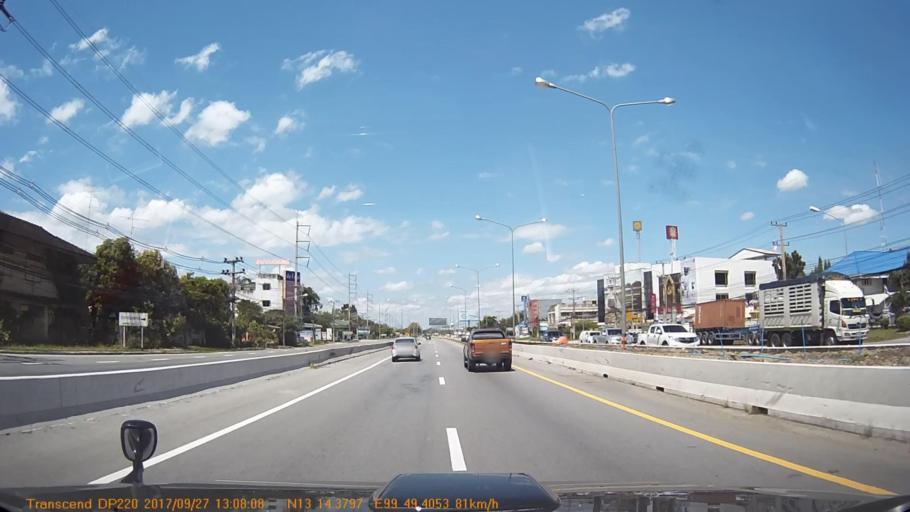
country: TH
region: Phetchaburi
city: Khao Yoi
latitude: 13.2398
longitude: 99.8235
